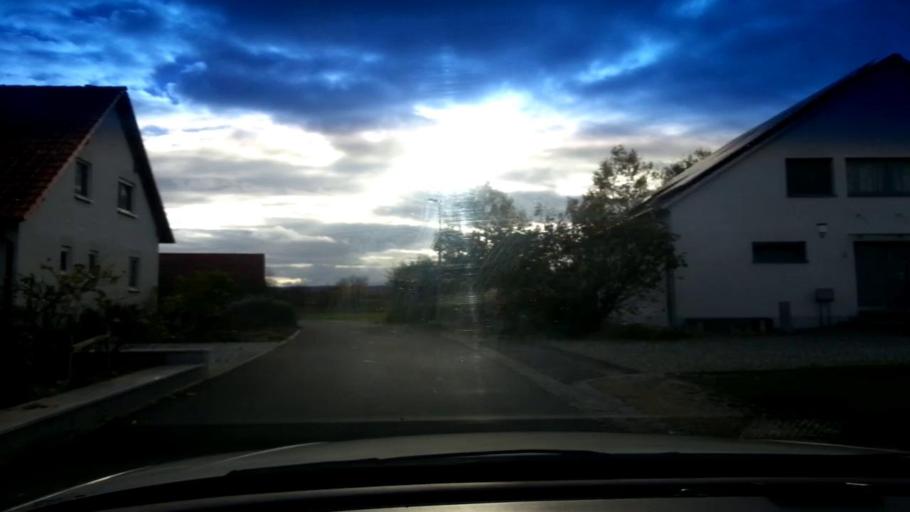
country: DE
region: Bavaria
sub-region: Upper Franconia
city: Rattelsdorf
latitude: 50.0062
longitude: 10.9004
